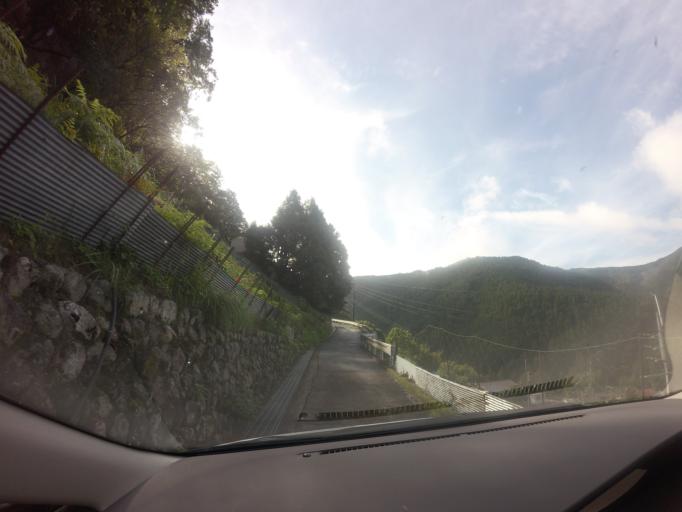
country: JP
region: Wakayama
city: Shingu
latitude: 33.9687
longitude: 135.8432
